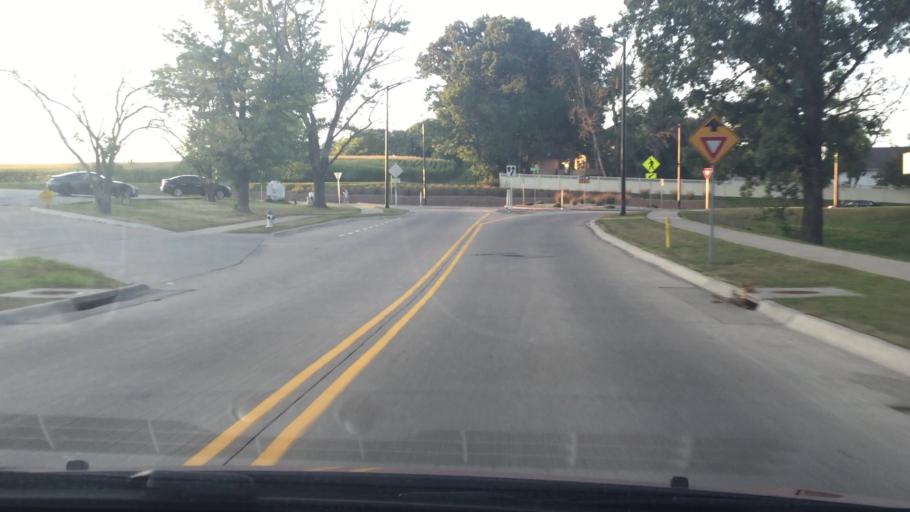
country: US
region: Iowa
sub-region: Muscatine County
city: Muscatine
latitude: 41.4350
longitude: -91.0648
